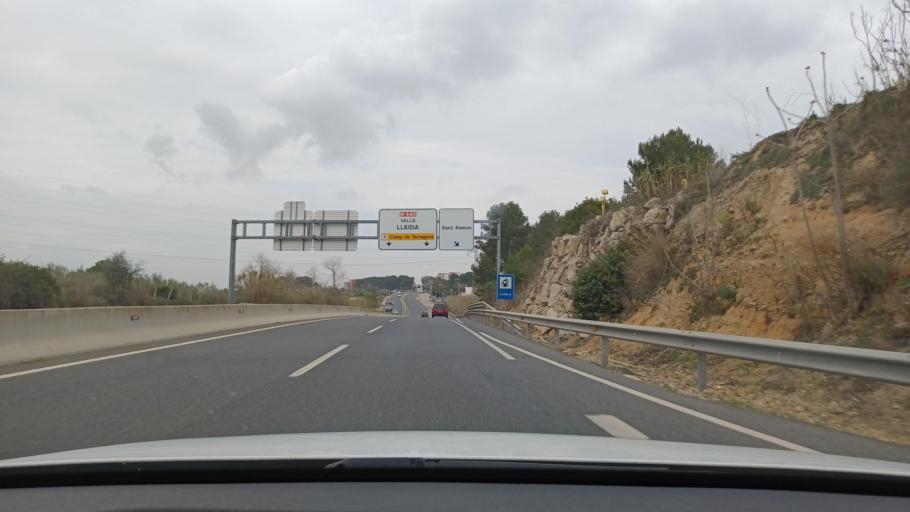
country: ES
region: Catalonia
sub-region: Provincia de Tarragona
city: Constanti
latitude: 41.1468
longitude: 1.2397
